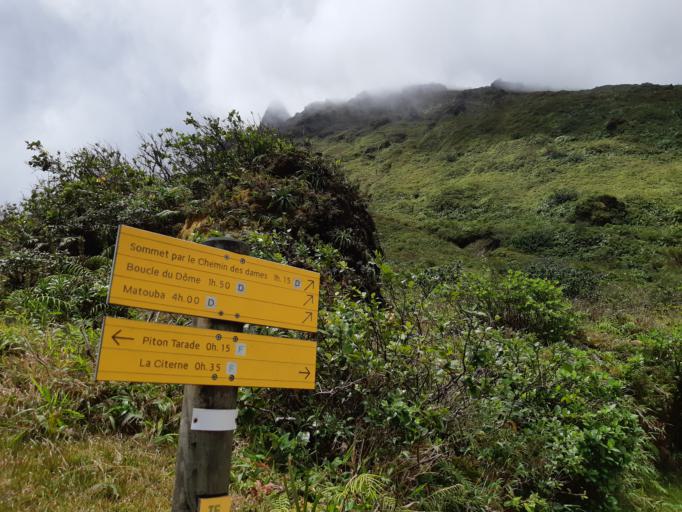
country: GP
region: Guadeloupe
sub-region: Guadeloupe
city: Saint-Claude
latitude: 16.0386
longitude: -61.6650
